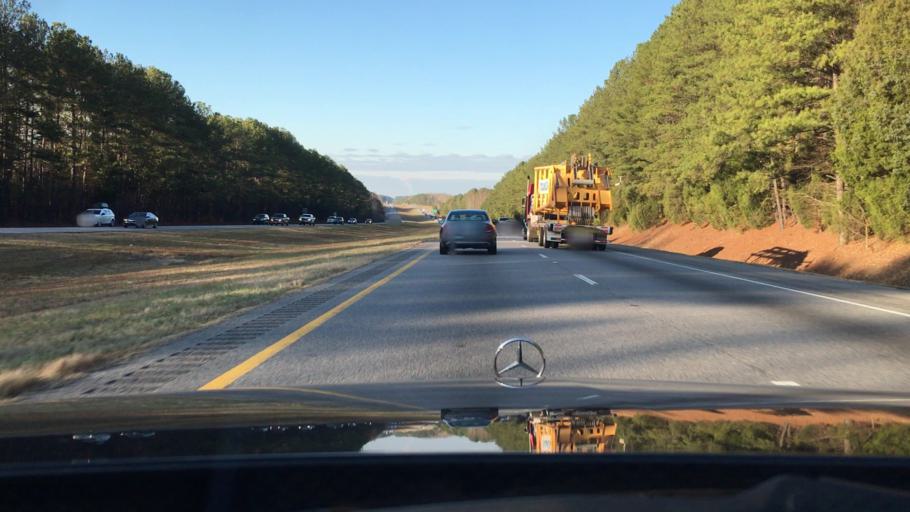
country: US
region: South Carolina
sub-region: Chester County
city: Eureka Mill
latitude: 34.6989
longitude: -81.0296
